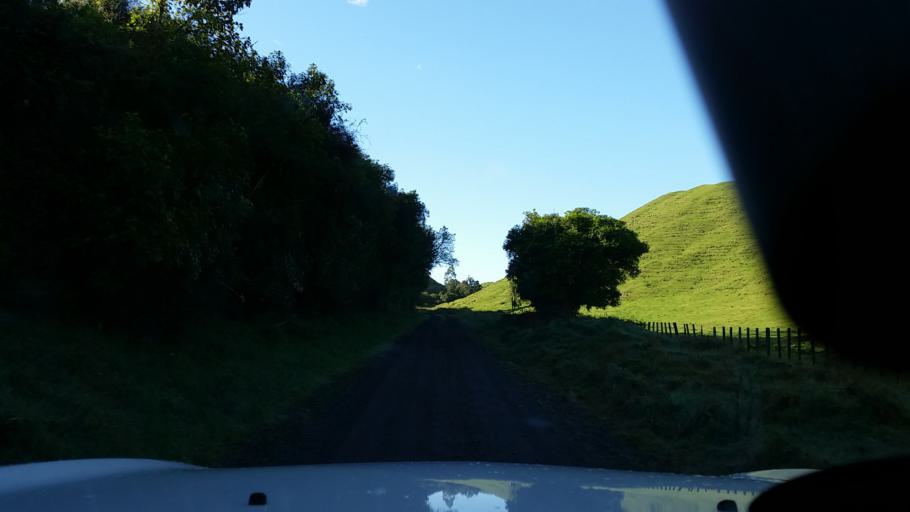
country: NZ
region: Bay of Plenty
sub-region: Kawerau District
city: Kawerau
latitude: -38.0111
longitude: 176.5667
